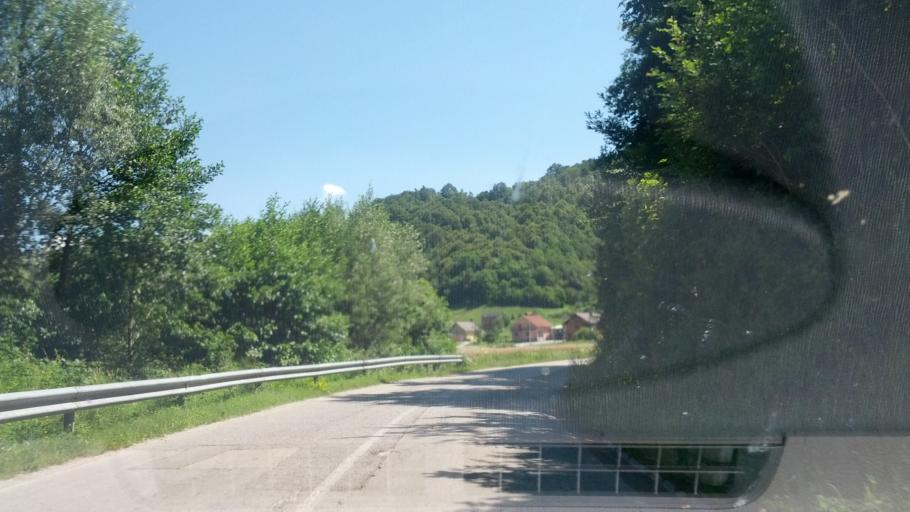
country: BA
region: Federation of Bosnia and Herzegovina
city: Otoka
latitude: 44.9877
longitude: 16.1604
